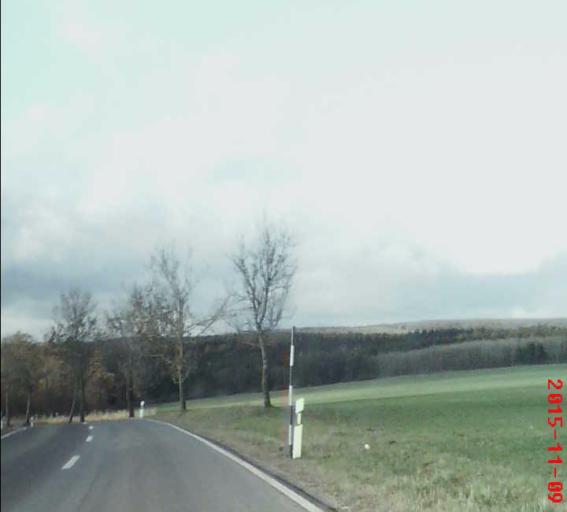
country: DE
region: Thuringia
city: Buttstedt
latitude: 51.2194
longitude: 10.2961
